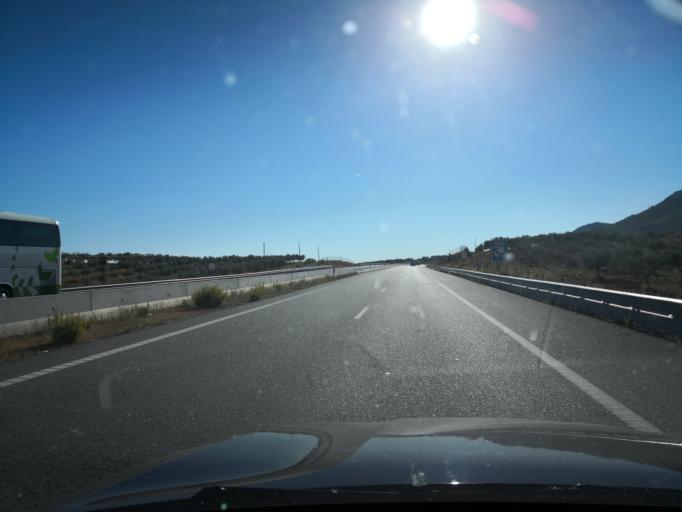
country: PT
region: Braganca
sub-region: Mirandela
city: Mirandela
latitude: 41.4659
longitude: -7.2441
